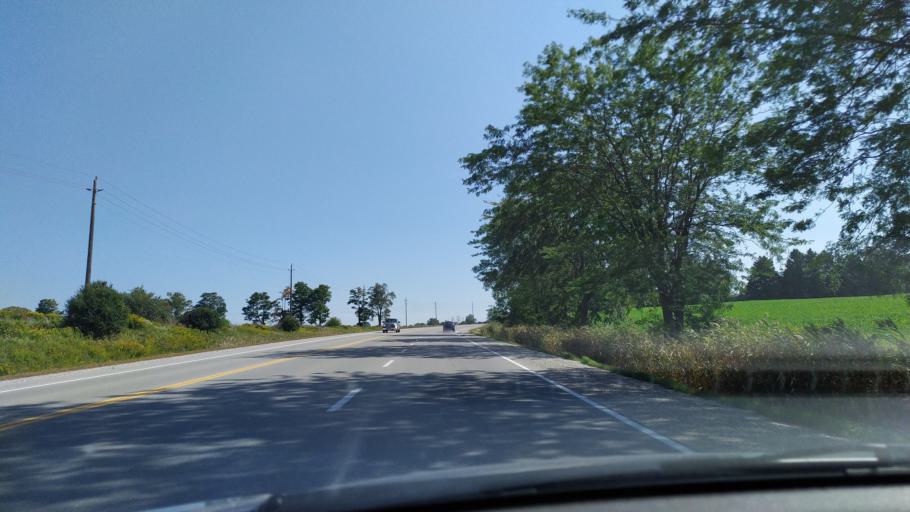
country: CA
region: Ontario
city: Ingersoll
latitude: 43.0657
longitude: -80.8419
